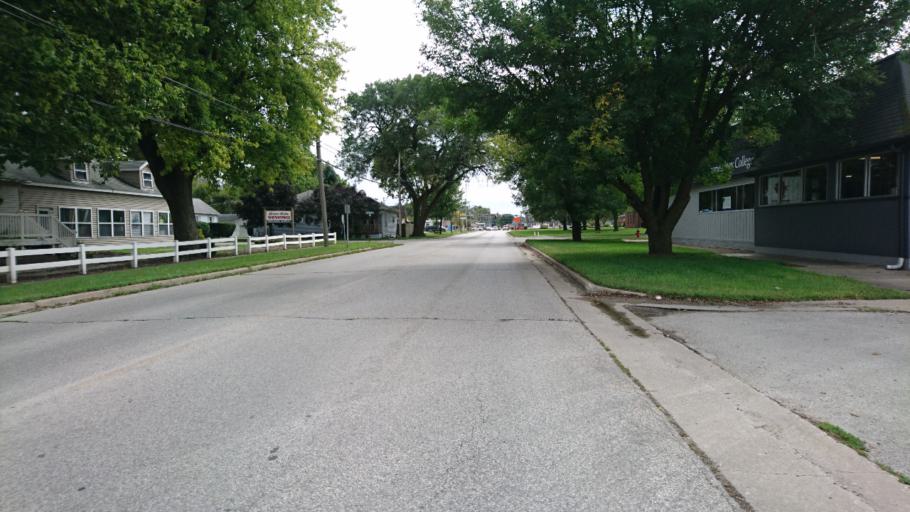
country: US
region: Illinois
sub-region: Livingston County
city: Pontiac
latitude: 40.8831
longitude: -88.6381
